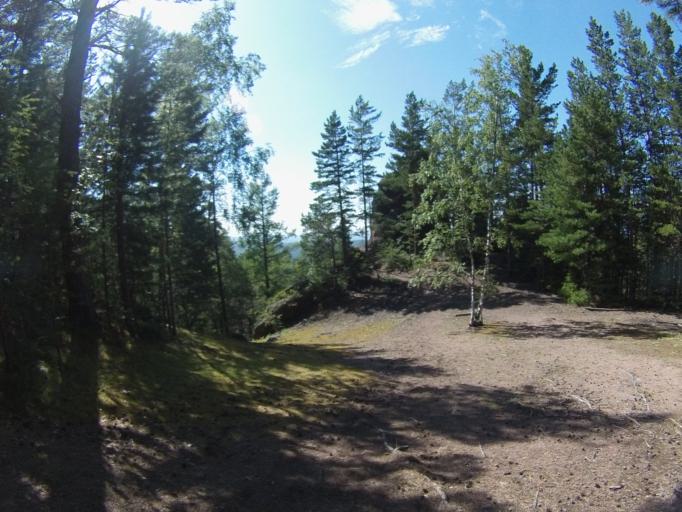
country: RU
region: Krasnoyarskiy
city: Krasnoyarsk
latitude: 55.9276
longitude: 92.7594
